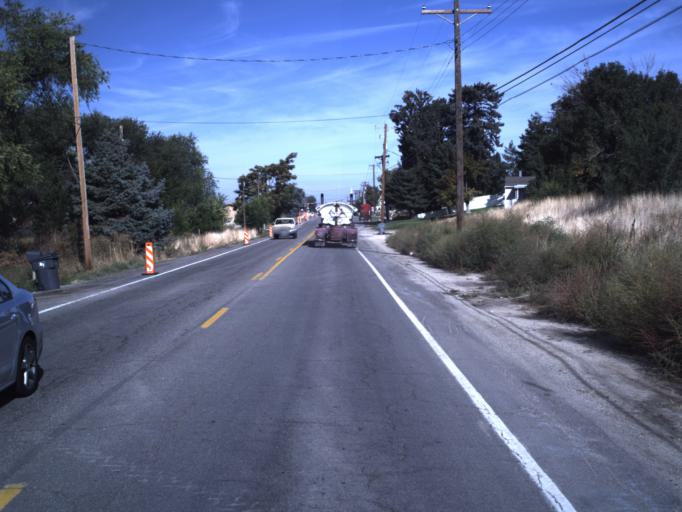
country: US
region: Utah
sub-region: Utah County
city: Orem
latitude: 40.2705
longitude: -111.7234
